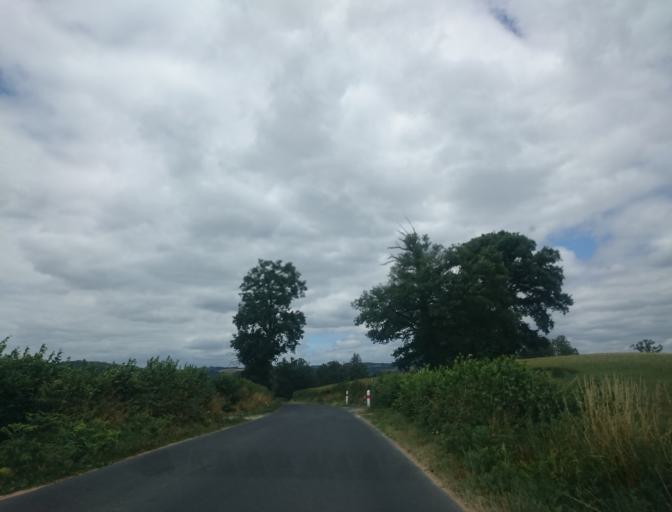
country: FR
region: Auvergne
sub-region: Departement du Cantal
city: Laroquebrou
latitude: 44.9503
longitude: 2.2014
